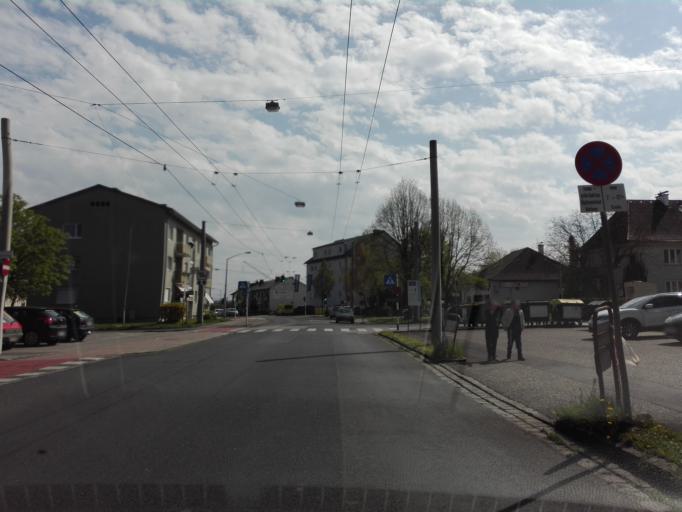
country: AT
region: Upper Austria
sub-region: Politischer Bezirk Linz-Land
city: Ansfelden
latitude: 48.2490
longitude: 14.2848
